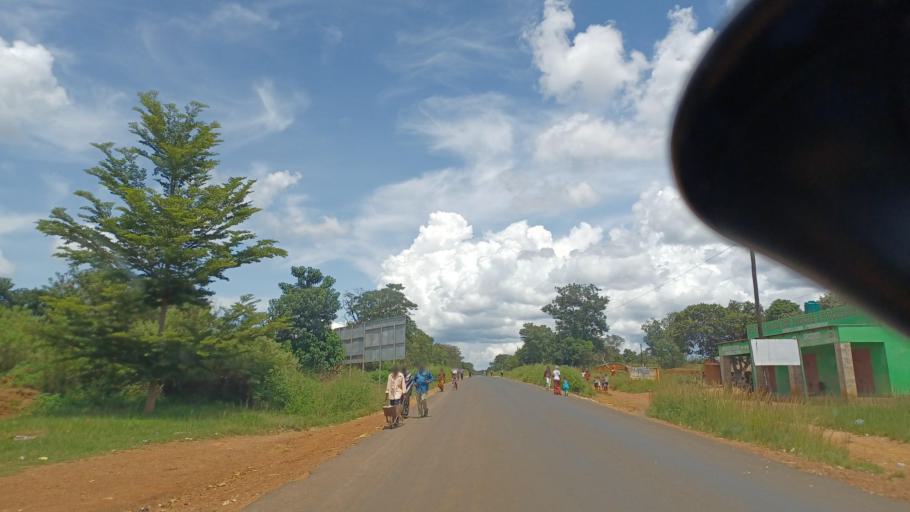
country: ZM
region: North-Western
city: Solwezi
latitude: -12.3963
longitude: 26.2383
